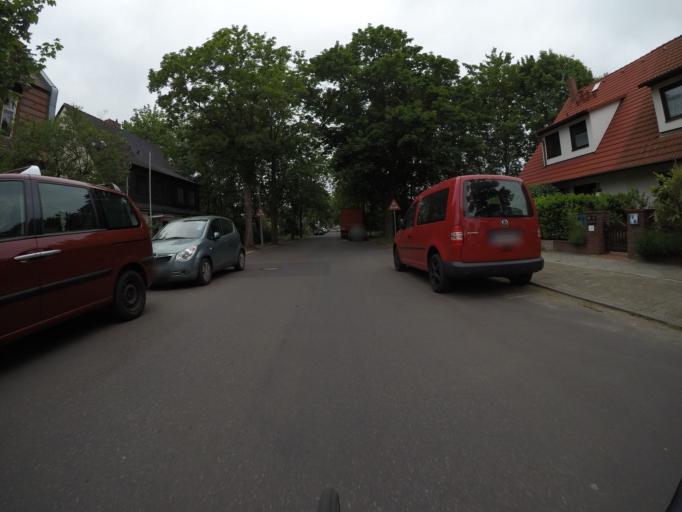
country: DE
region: Berlin
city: Lubars
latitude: 52.6084
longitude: 13.3414
